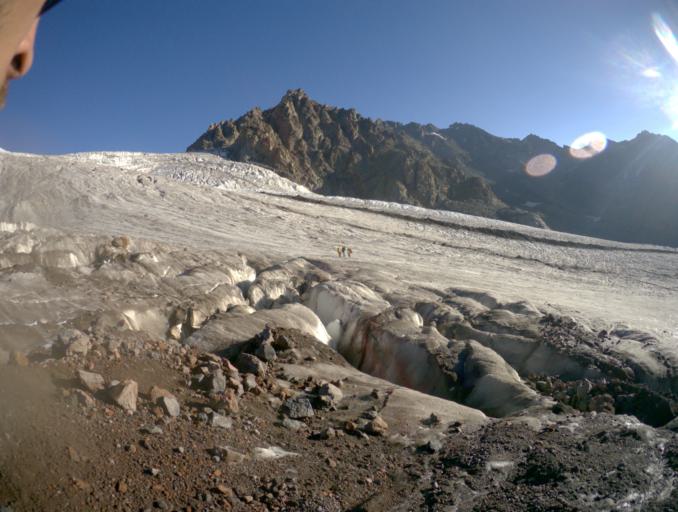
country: RU
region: Kabardino-Balkariya
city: Terskol
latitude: 43.3184
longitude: 42.5183
